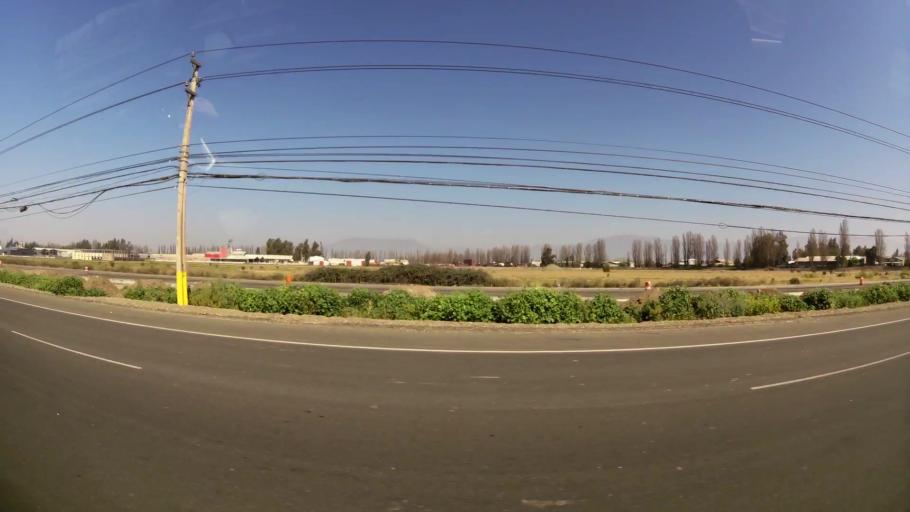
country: CL
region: Santiago Metropolitan
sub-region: Provincia de Chacabuco
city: Chicureo Abajo
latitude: -33.2855
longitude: -70.7366
